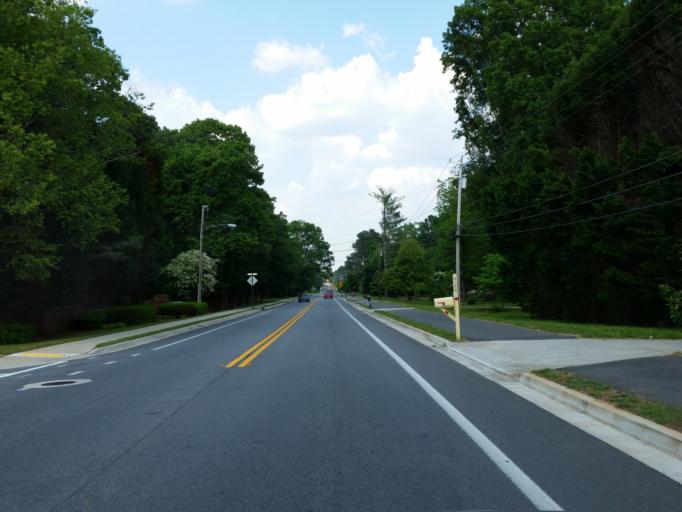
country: US
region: Georgia
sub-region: Fulton County
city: Sandy Springs
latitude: 33.9687
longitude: -84.4006
